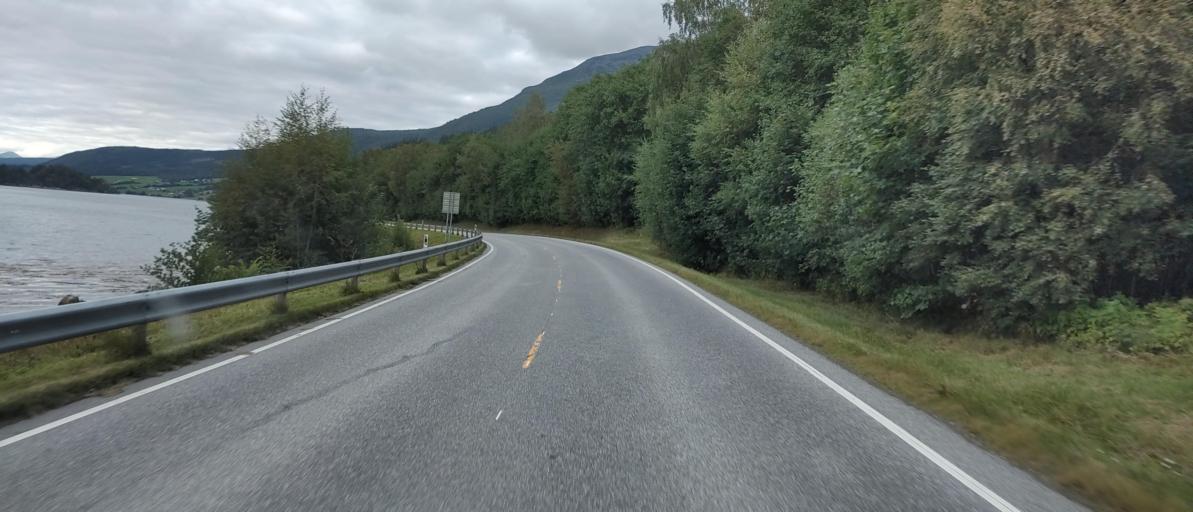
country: NO
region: More og Romsdal
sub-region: Rauma
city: Andalsnes
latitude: 62.5903
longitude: 7.5455
